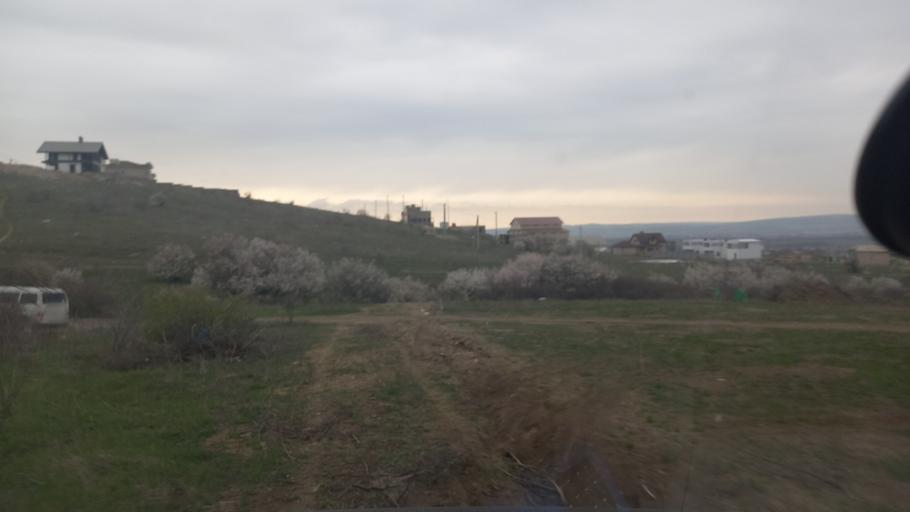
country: RU
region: Krasnodarskiy
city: Anapa
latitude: 44.8533
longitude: 37.3444
